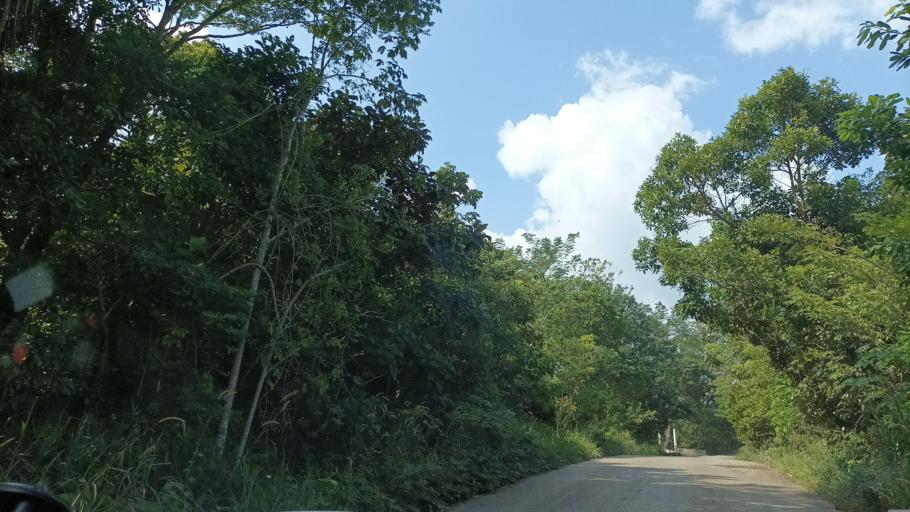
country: MX
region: Veracruz
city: Las Choapas
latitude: 17.7488
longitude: -94.1097
